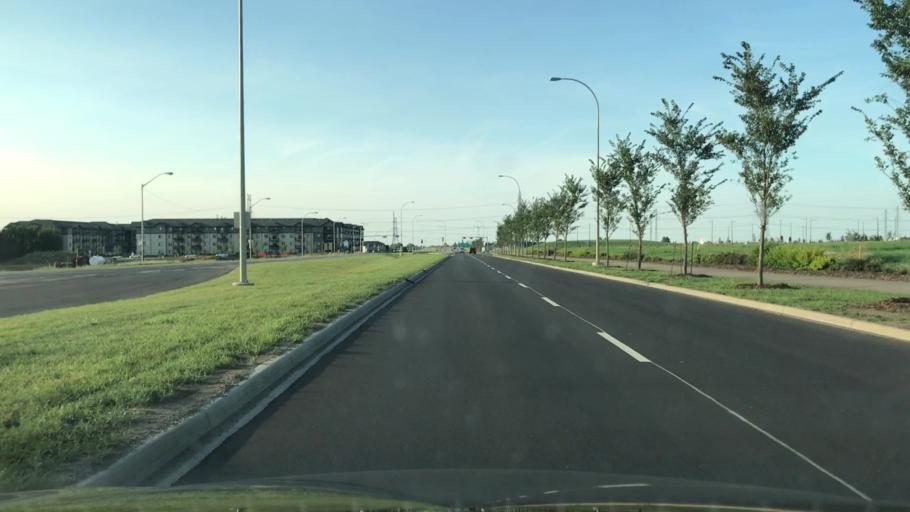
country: CA
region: Alberta
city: Beaumont
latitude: 53.4255
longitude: -113.4177
